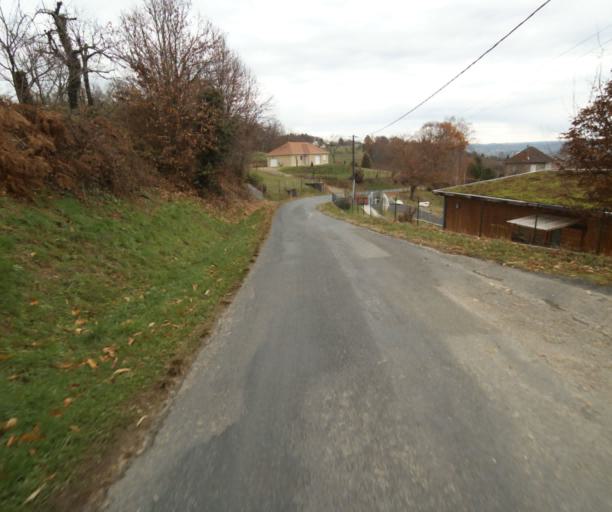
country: FR
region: Limousin
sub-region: Departement de la Correze
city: Chameyrat
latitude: 45.2582
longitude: 1.7287
